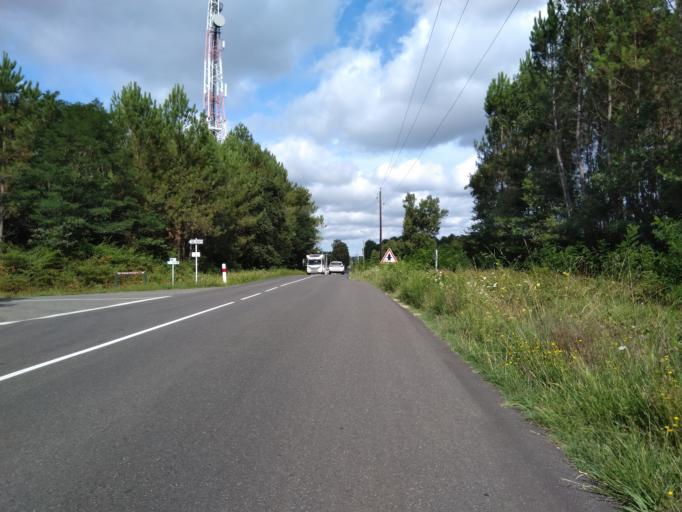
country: FR
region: Aquitaine
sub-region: Departement des Landes
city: Mees
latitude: 43.7336
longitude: -1.1056
